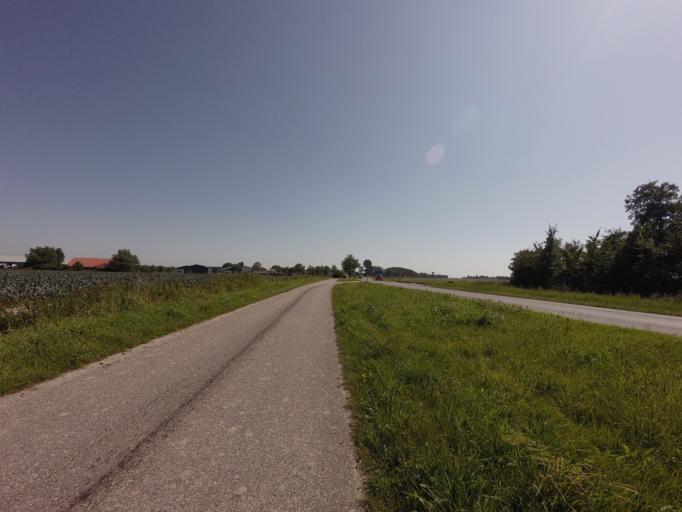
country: NL
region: Friesland
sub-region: Gemeente Dongeradeel
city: Dokkum
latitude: 53.3807
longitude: 6.0402
